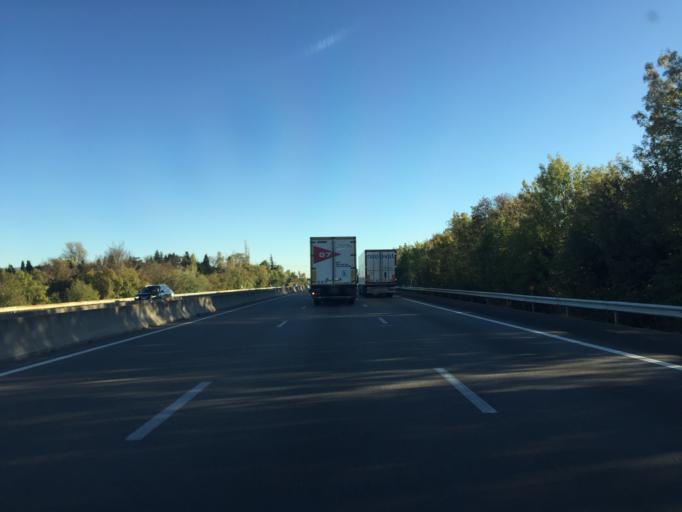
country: FR
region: Provence-Alpes-Cote d'Azur
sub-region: Departement des Bouches-du-Rhone
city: Senas
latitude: 43.7309
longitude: 5.0894
